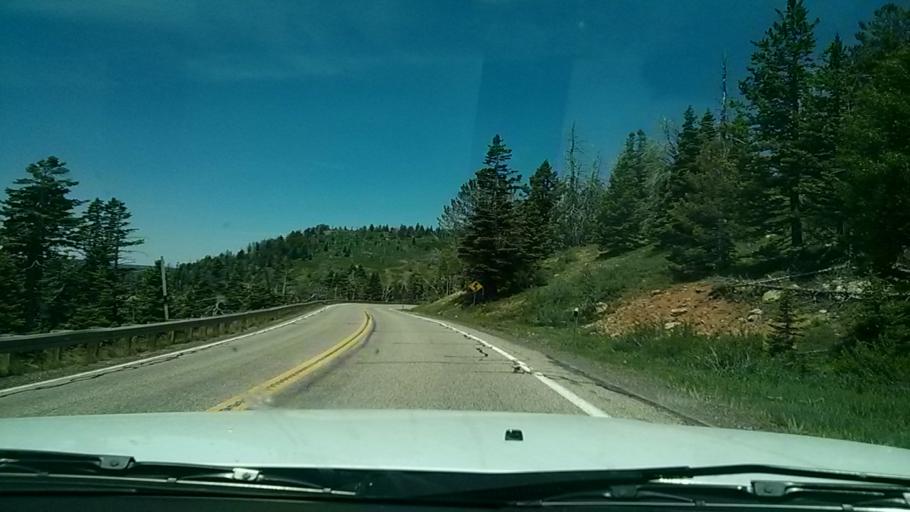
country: US
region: Utah
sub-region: Iron County
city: Cedar City
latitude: 37.5780
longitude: -112.8697
